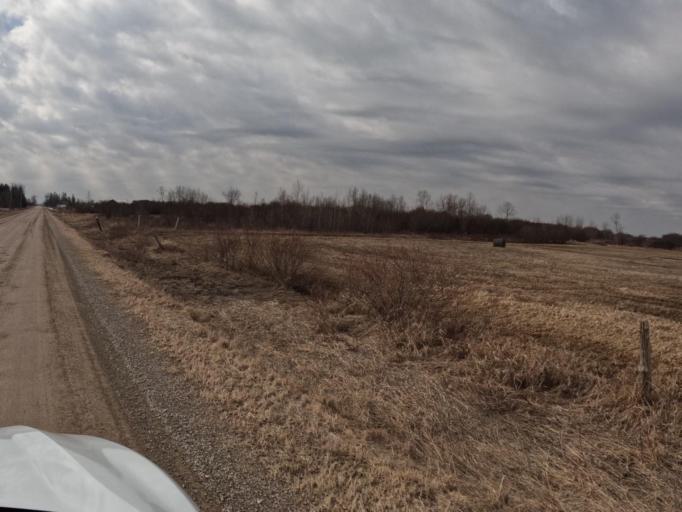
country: CA
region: Ontario
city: Orangeville
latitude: 43.9178
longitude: -80.2173
